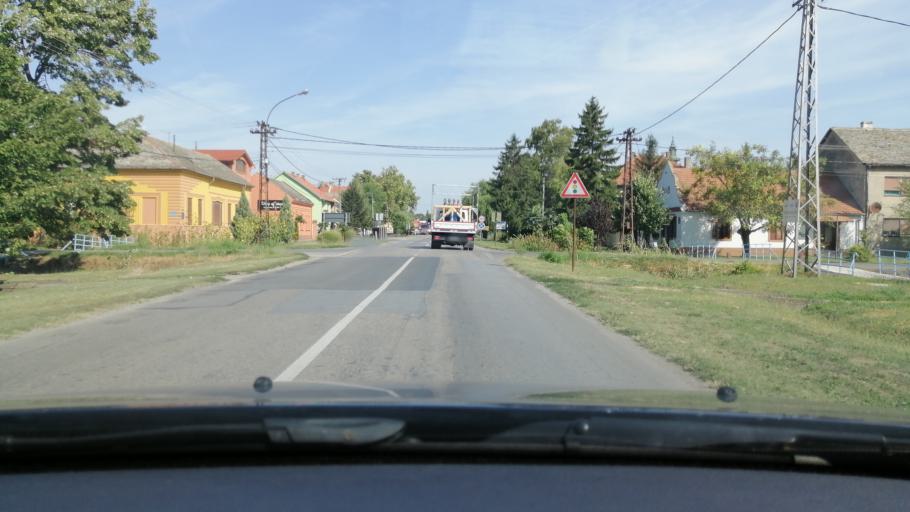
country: RS
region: Autonomna Pokrajina Vojvodina
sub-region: Juznobanatski Okrug
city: Kovacica
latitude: 45.1097
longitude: 20.6190
